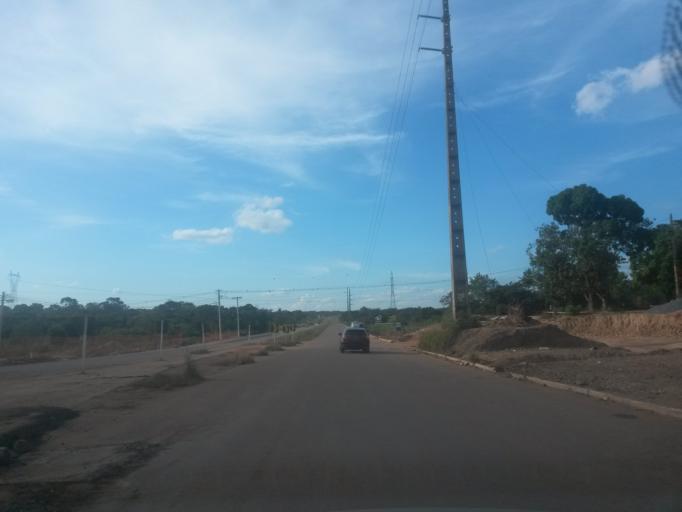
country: BR
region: Mato Grosso
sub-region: Cuiaba
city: Cuiaba
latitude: -15.5333
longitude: -56.0752
